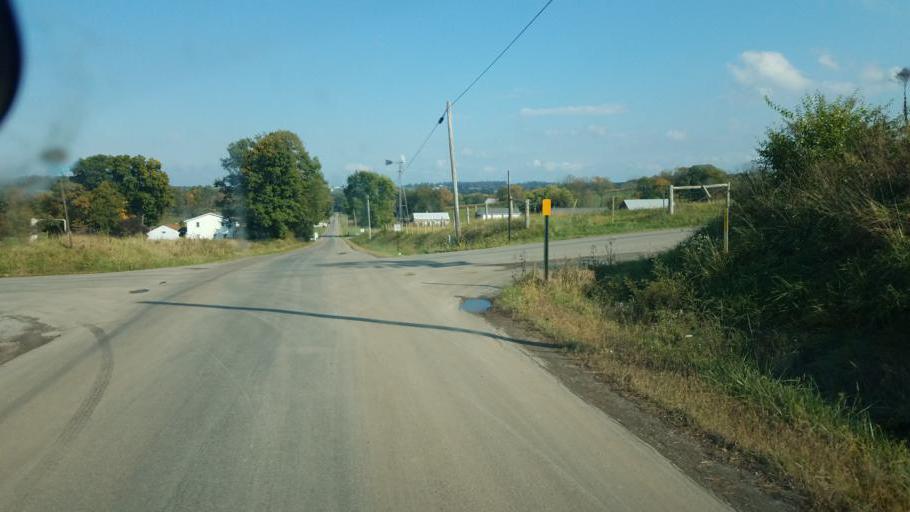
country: US
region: Ohio
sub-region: Wayne County
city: Apple Creek
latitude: 40.6751
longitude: -81.8423
